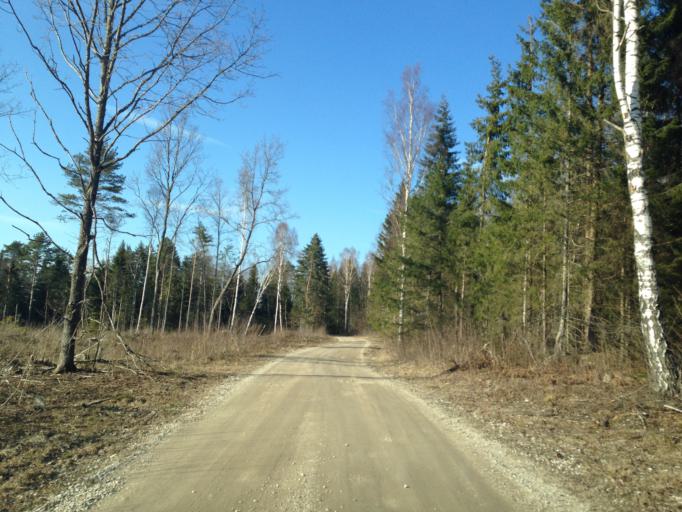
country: EE
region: Harju
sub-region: Nissi vald
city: Turba
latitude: 59.1257
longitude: 24.1663
